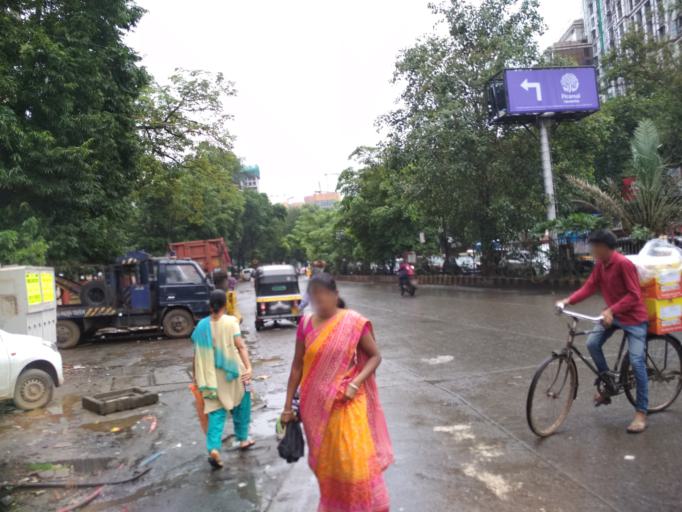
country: IN
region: Maharashtra
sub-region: Thane
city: Thane
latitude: 19.1639
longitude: 72.9377
